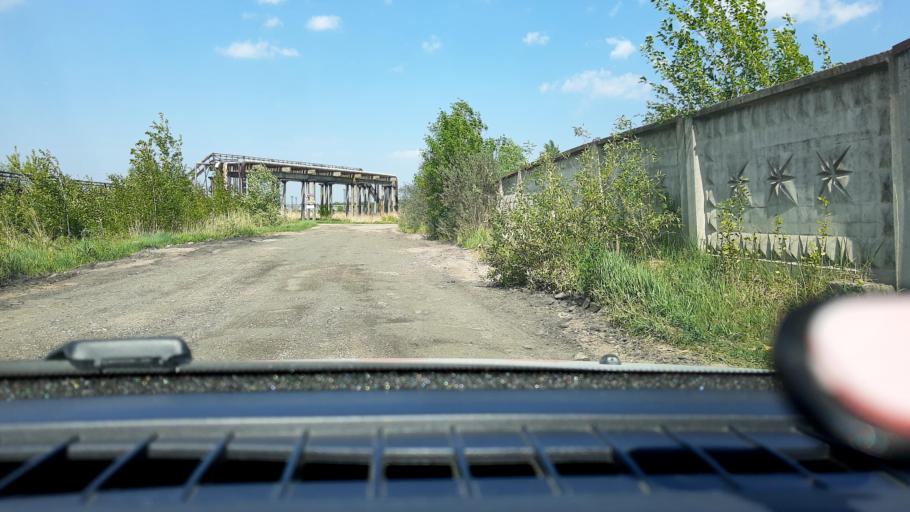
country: RU
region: Nizjnij Novgorod
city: Kstovo
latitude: 56.1335
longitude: 44.1268
